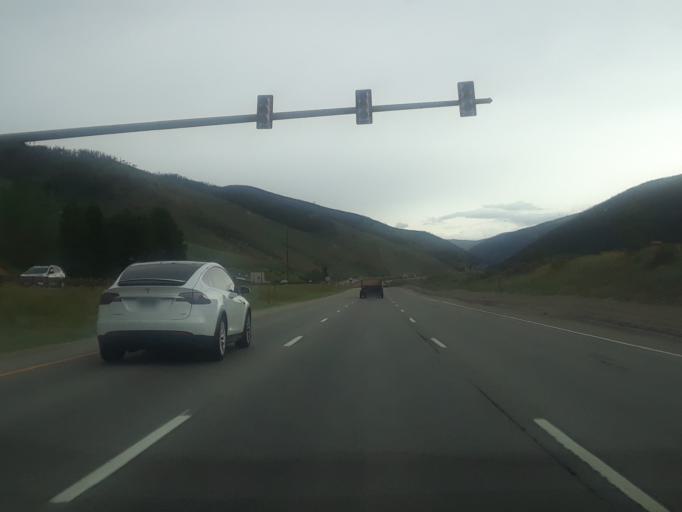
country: US
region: Colorado
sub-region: Summit County
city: Silverthorne
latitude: 39.6396
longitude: -106.0455
